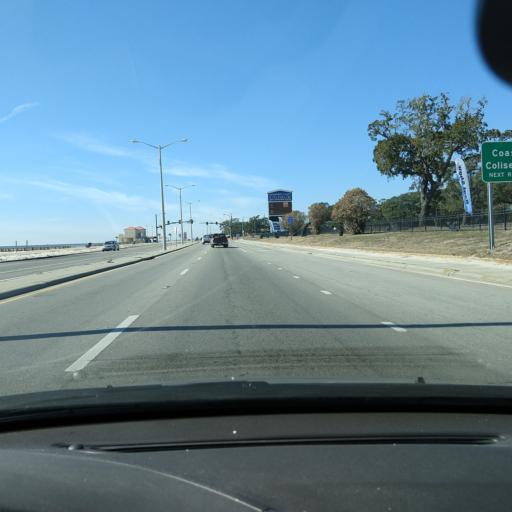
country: US
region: Mississippi
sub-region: Harrison County
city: Biloxi
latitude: 30.3914
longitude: -88.9731
